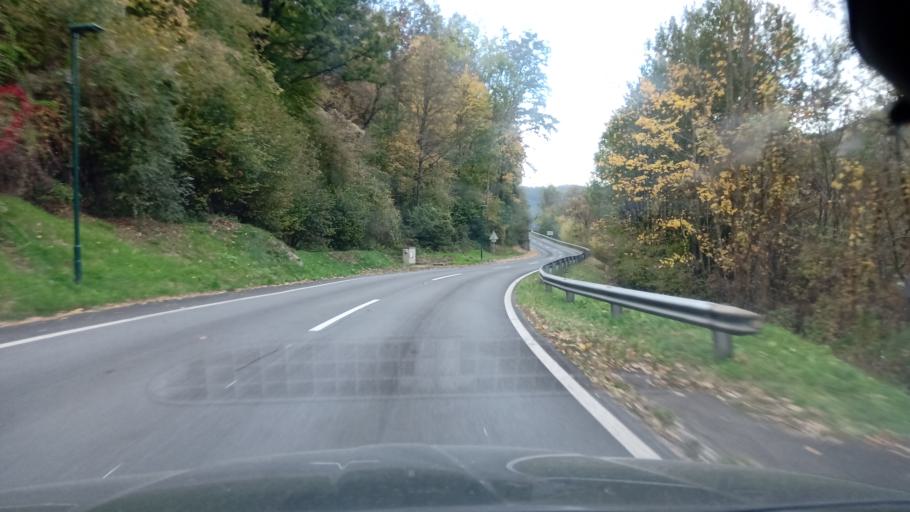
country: AT
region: Styria
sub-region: Politischer Bezirk Leoben
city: Proleb
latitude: 47.3944
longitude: 15.1271
